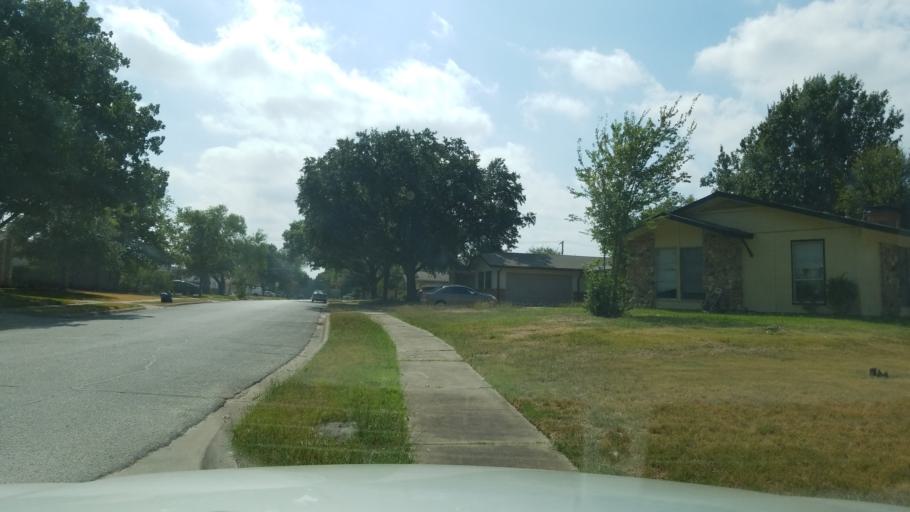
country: US
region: Texas
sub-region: Dallas County
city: Garland
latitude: 32.8922
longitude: -96.6629
